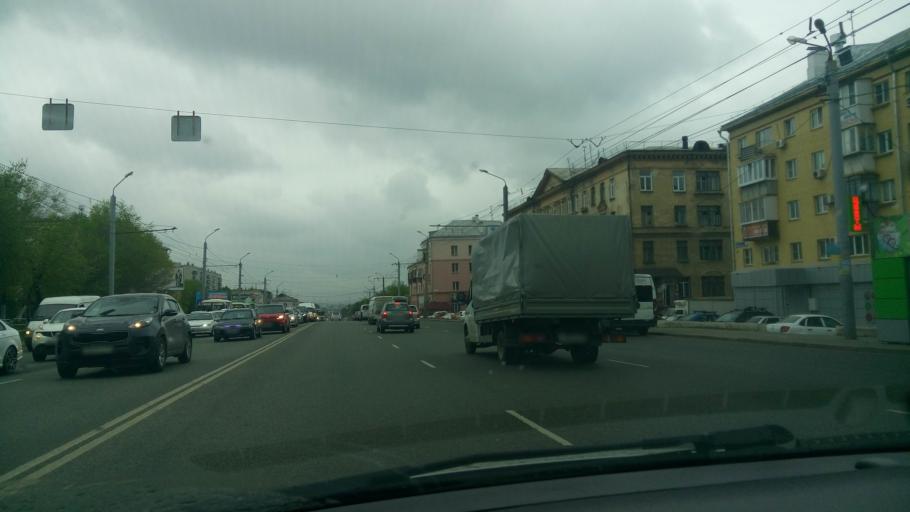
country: RU
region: Chelyabinsk
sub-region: Gorod Chelyabinsk
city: Chelyabinsk
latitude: 55.1852
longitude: 61.3869
